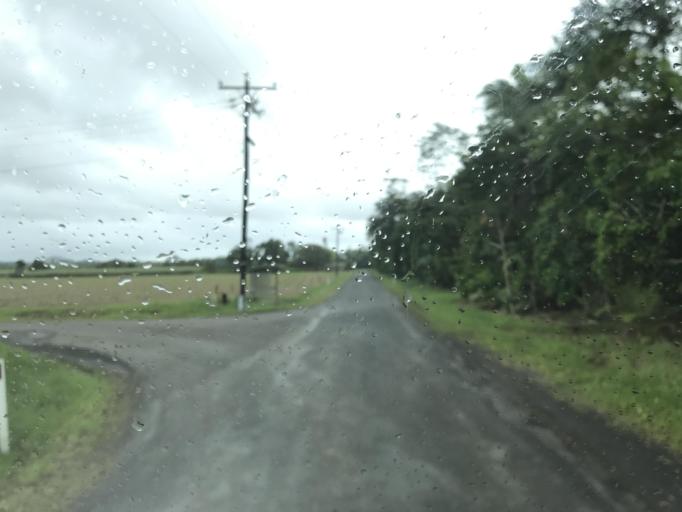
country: AU
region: Queensland
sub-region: Cassowary Coast
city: Innisfail
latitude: -17.4953
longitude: 145.9880
